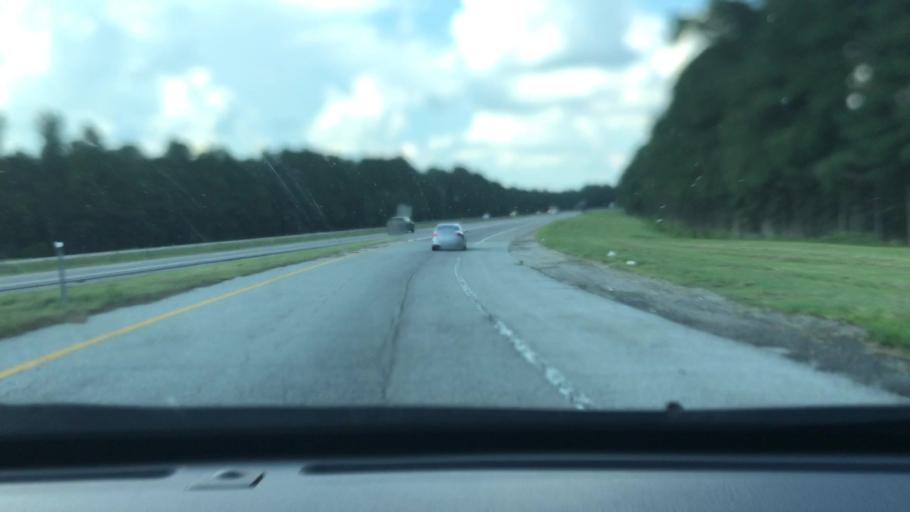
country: US
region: South Carolina
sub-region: Sumter County
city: East Sumter
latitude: 33.9026
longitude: -80.0919
